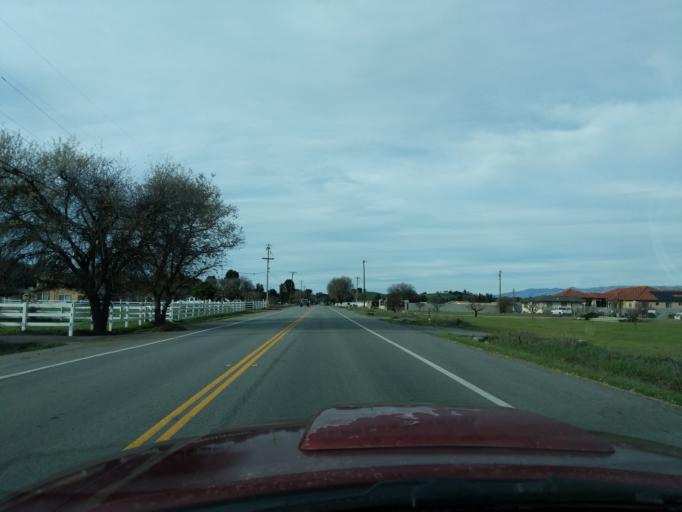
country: US
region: California
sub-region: Santa Clara County
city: San Martin
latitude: 37.0761
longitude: -121.6202
